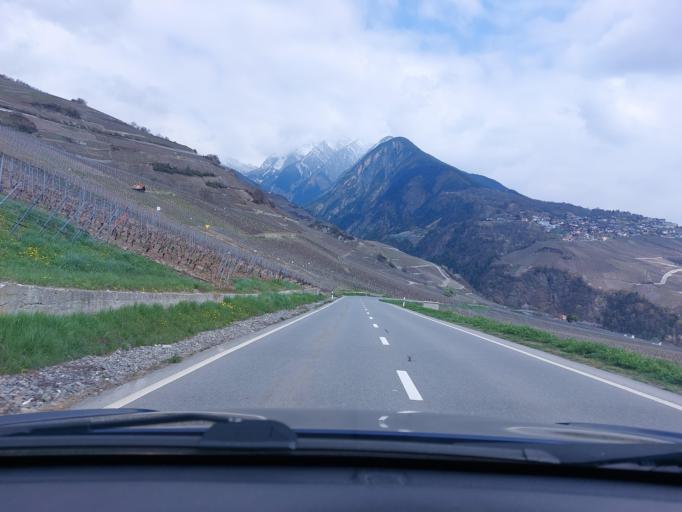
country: CH
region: Valais
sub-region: Conthey District
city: Conthey
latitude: 46.2406
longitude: 7.3003
